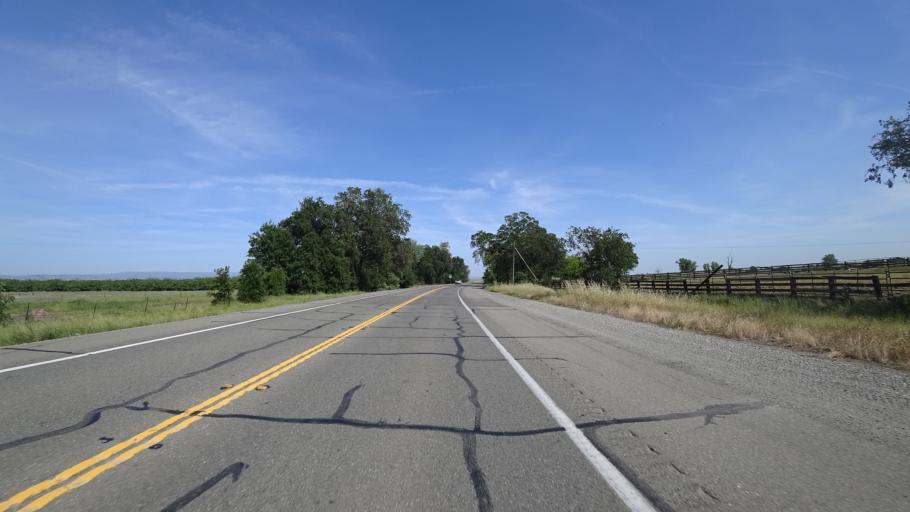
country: US
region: California
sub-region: Tehama County
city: Los Molinos
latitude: 39.9374
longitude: -122.0409
